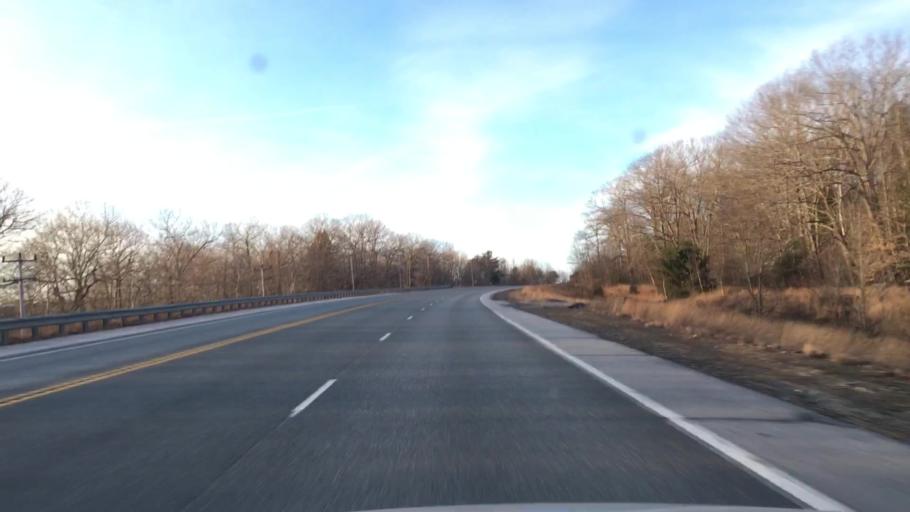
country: US
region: Maine
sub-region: Hancock County
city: Dedham
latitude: 44.6967
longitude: -68.5943
